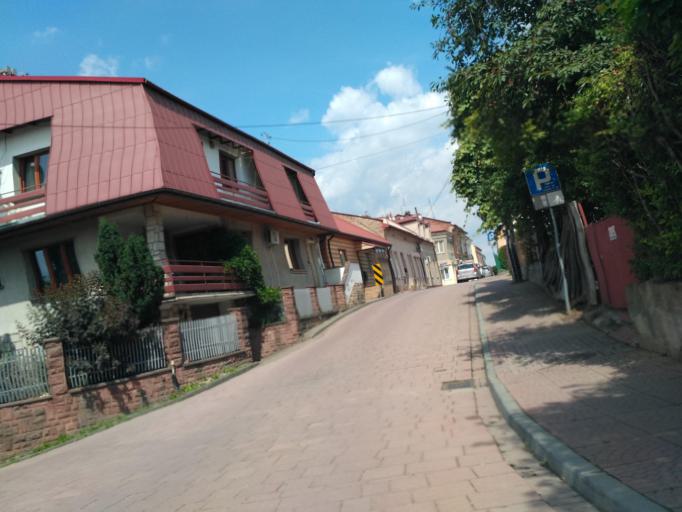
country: PL
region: Subcarpathian Voivodeship
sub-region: Powiat debicki
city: Pilzno
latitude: 49.9772
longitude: 21.2915
